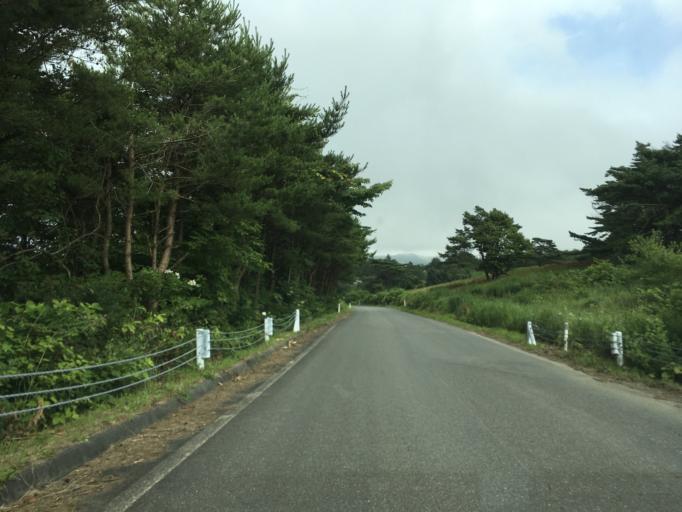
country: JP
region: Iwate
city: Ofunato
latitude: 38.9836
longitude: 141.4490
